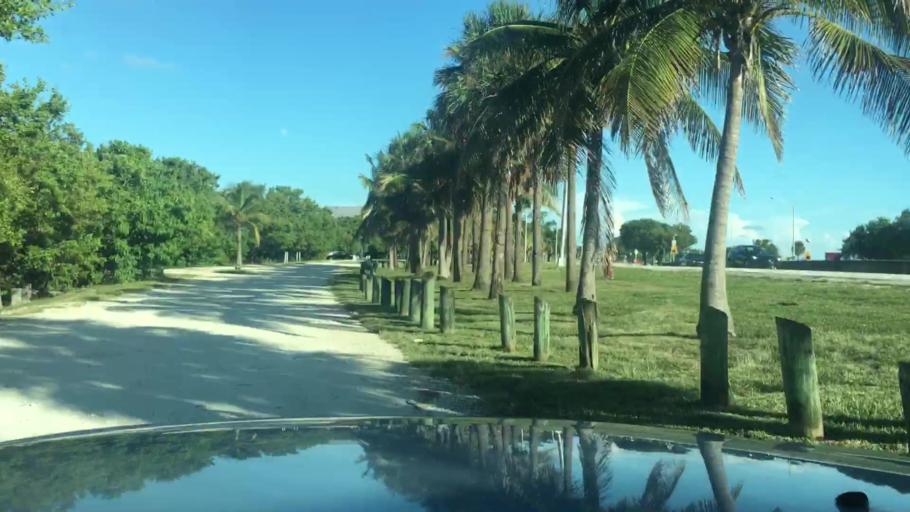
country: US
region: Florida
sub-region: Miami-Dade County
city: Miami
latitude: 25.7463
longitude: -80.1764
